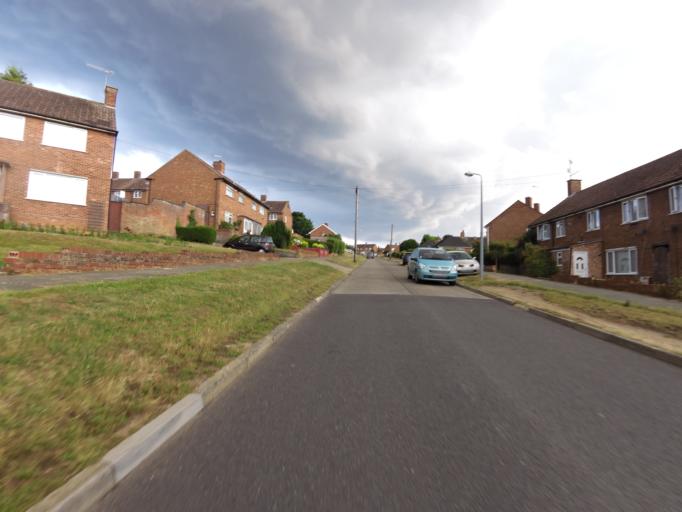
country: GB
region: England
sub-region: Suffolk
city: Ipswich
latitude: 52.0503
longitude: 1.1316
